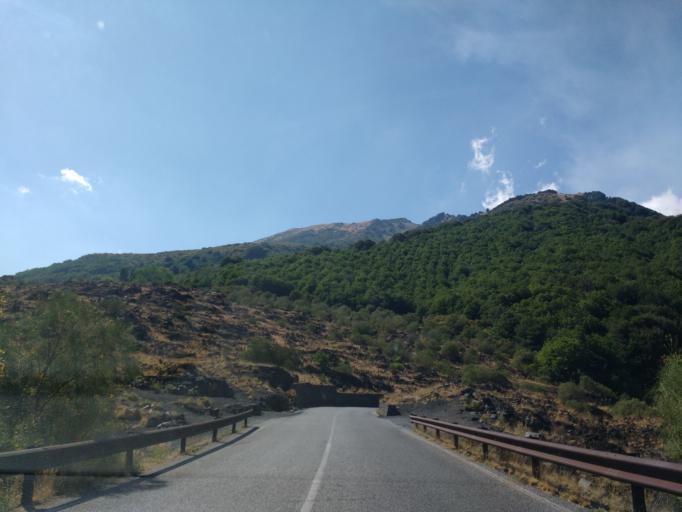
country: IT
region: Sicily
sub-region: Catania
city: Zafferana Etnea
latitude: 37.6987
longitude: 15.0500
